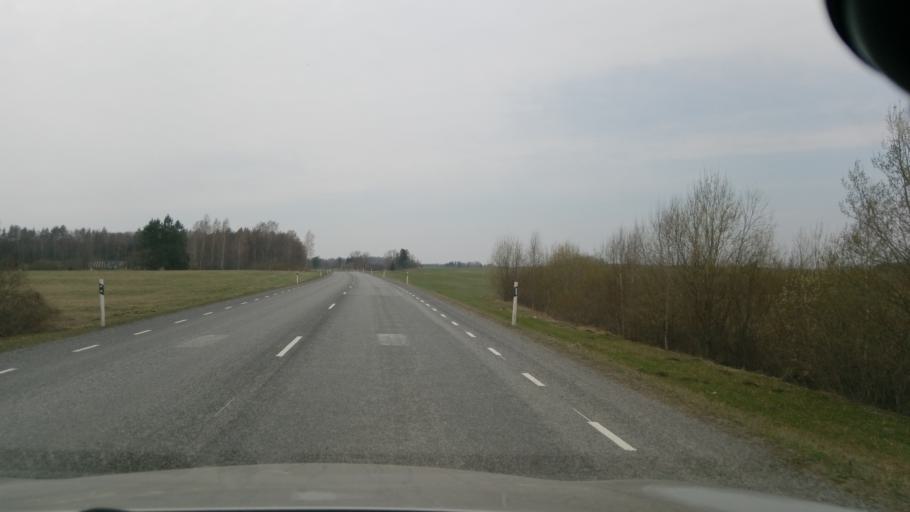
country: EE
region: Jaervamaa
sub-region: Tueri vald
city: Sarevere
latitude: 58.7765
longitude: 25.5060
